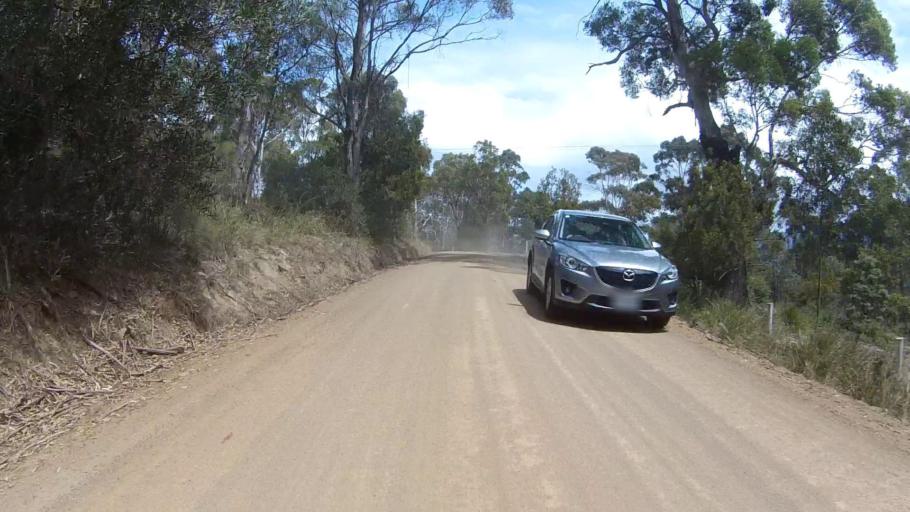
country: AU
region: Tasmania
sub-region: Kingborough
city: Blackmans Bay
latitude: -43.0462
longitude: 147.3077
